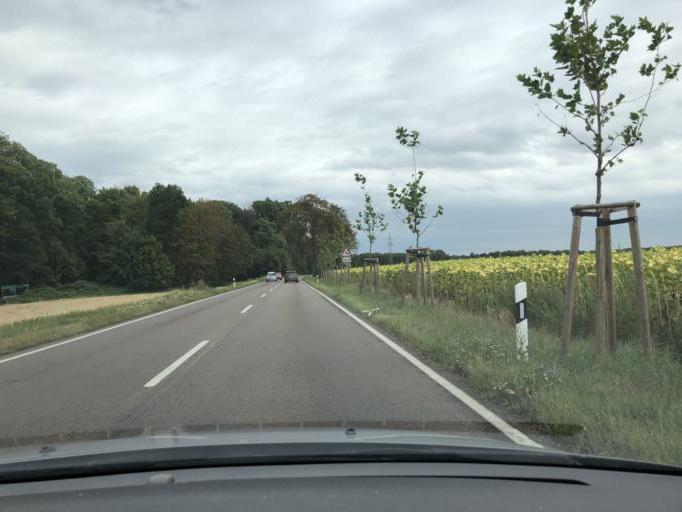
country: DE
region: Saxony-Anhalt
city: Koethen
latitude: 51.7589
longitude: 11.9366
